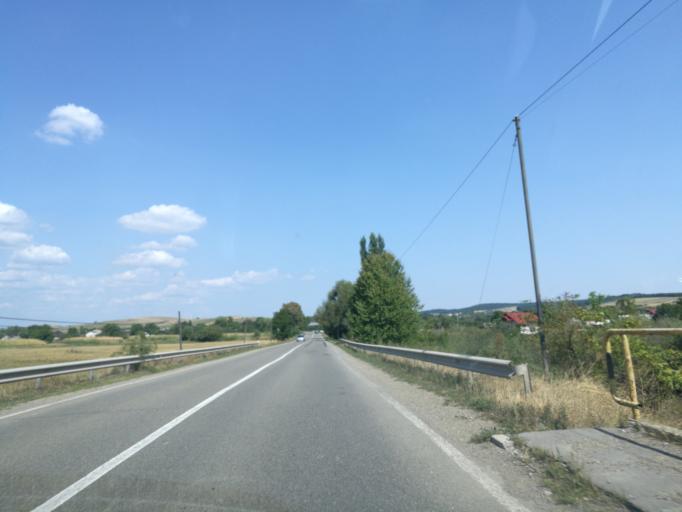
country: RO
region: Neamt
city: Bodesti
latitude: 47.0475
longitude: 26.4041
